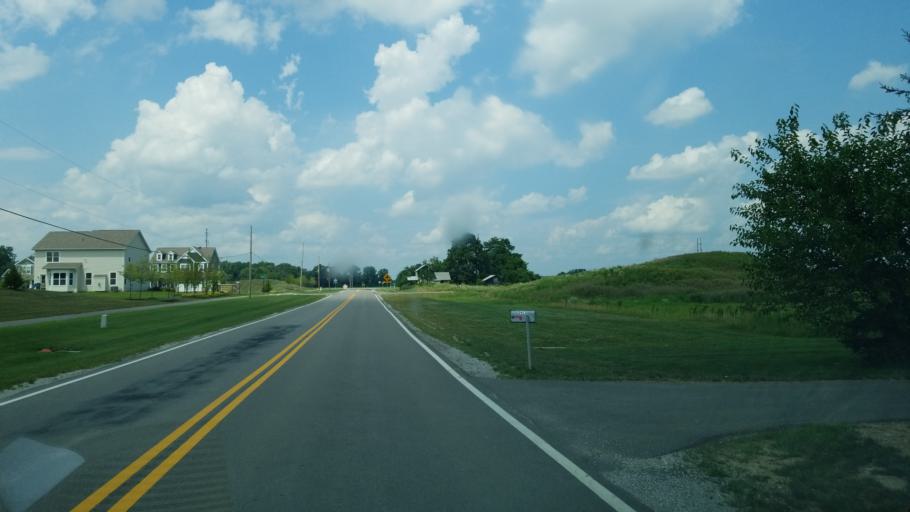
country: US
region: Ohio
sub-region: Delaware County
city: Lewis Center
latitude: 40.2099
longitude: -83.0134
